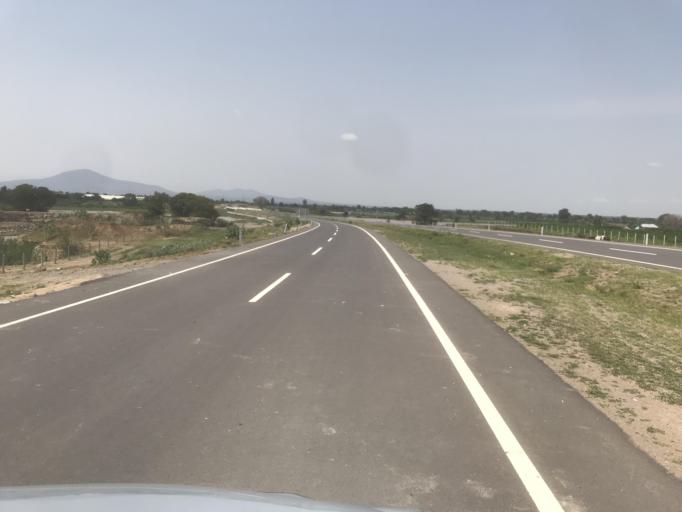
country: ET
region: Oromiya
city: Mojo
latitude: 8.4098
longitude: 39.0129
